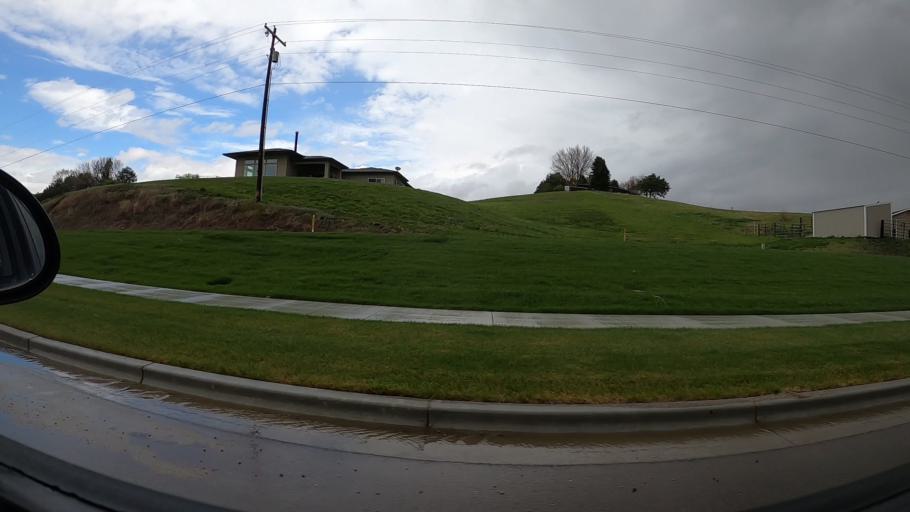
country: US
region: Idaho
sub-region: Ada County
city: Eagle
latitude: 43.7354
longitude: -116.2919
